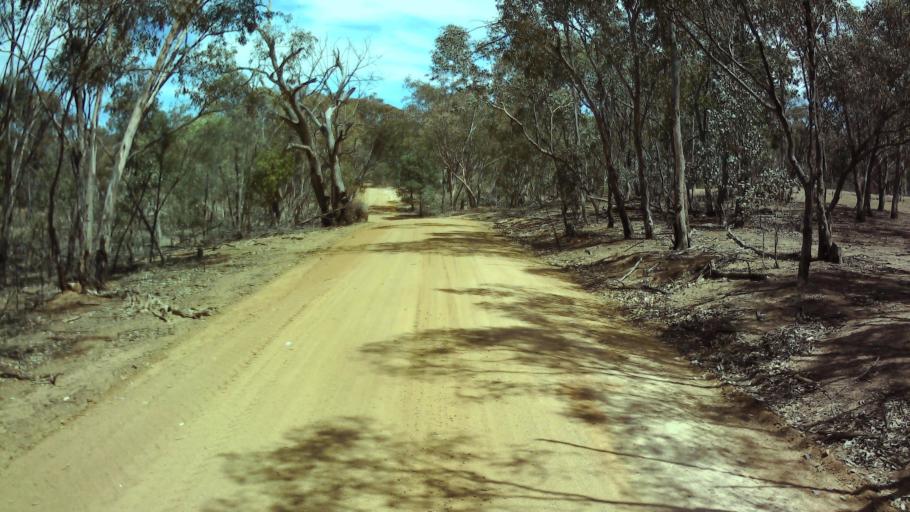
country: AU
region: New South Wales
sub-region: Weddin
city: Grenfell
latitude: -33.8011
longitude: 148.1598
